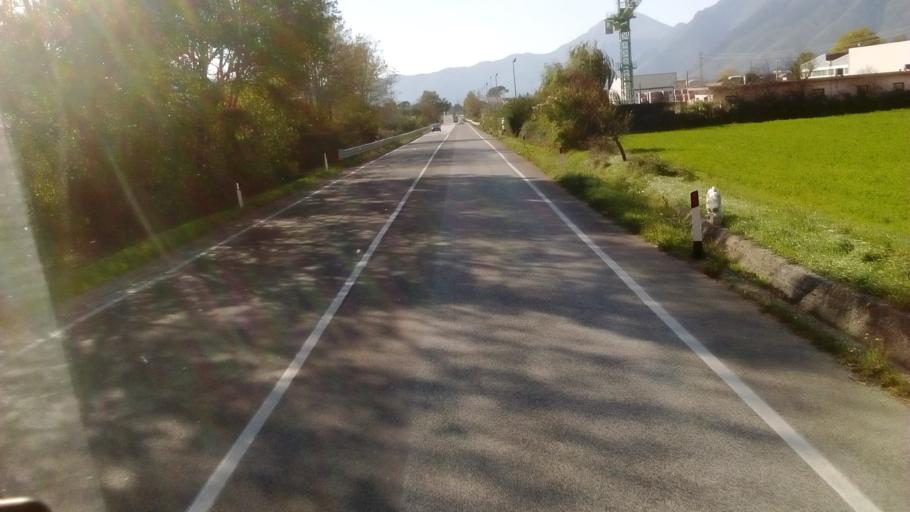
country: IT
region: Molise
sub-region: Provincia di Isernia
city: Taverna Ravindola
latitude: 41.5061
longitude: 14.1074
